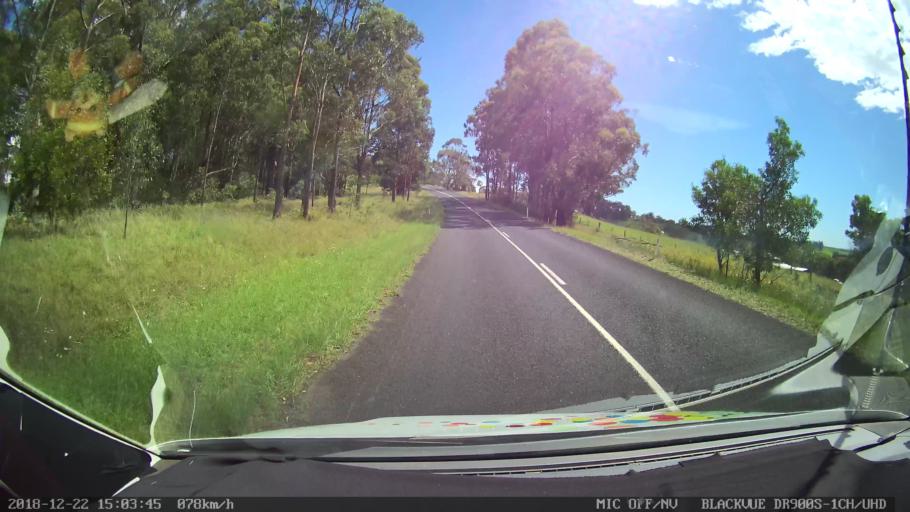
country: AU
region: New South Wales
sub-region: Bellingen
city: Dorrigo
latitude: -30.2677
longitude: 152.4391
